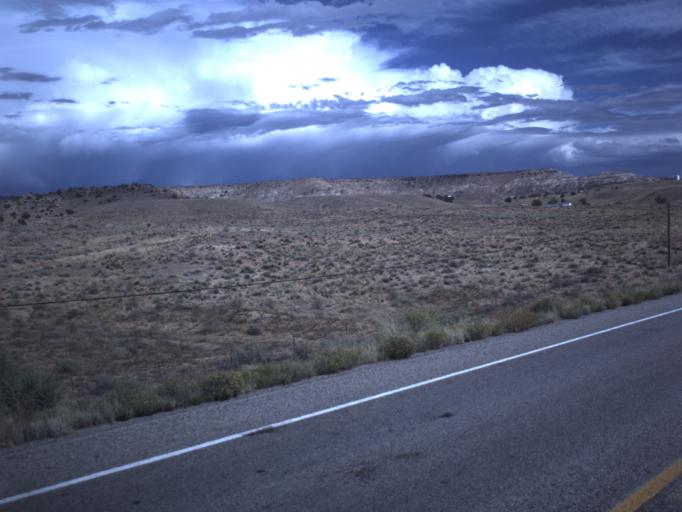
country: US
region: Colorado
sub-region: Montezuma County
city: Towaoc
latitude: 37.2053
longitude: -109.1619
